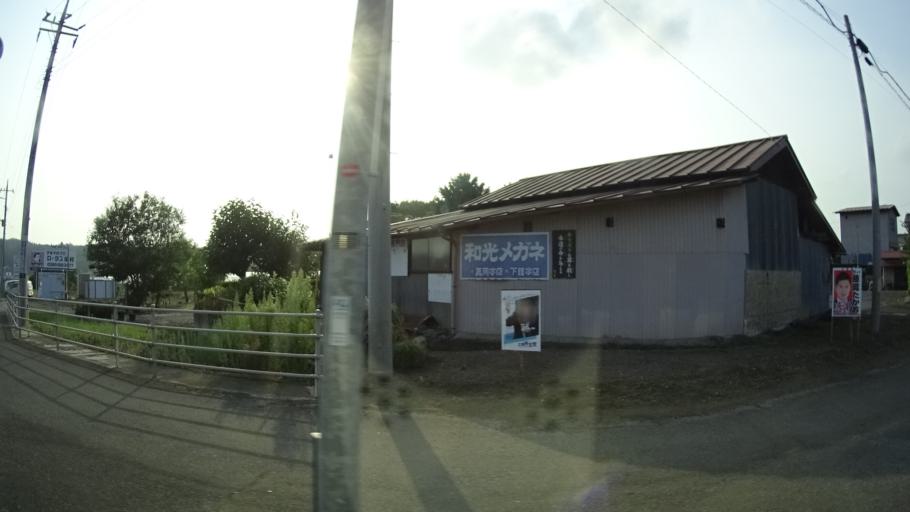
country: JP
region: Tochigi
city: Mashiko
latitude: 36.5459
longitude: 140.1036
